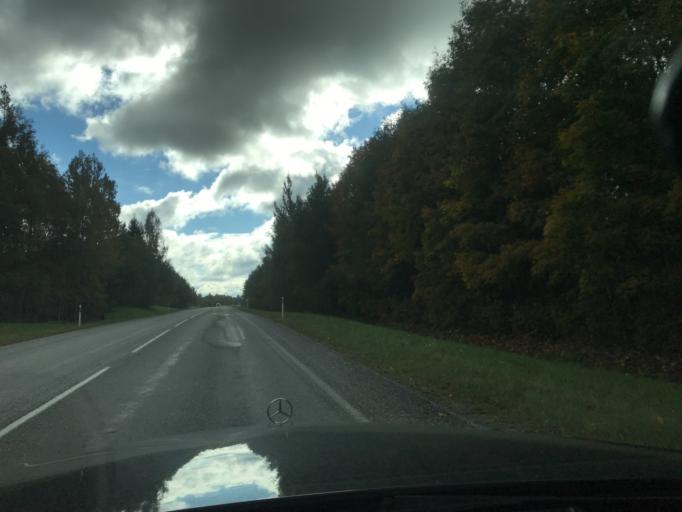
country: RU
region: Pskov
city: Pechory
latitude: 57.6998
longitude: 27.3254
